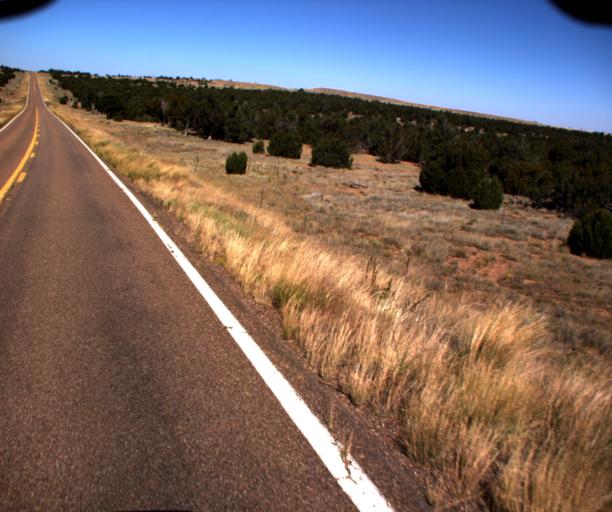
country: US
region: Arizona
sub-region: Navajo County
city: Heber-Overgaard
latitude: 34.4581
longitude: -110.4661
